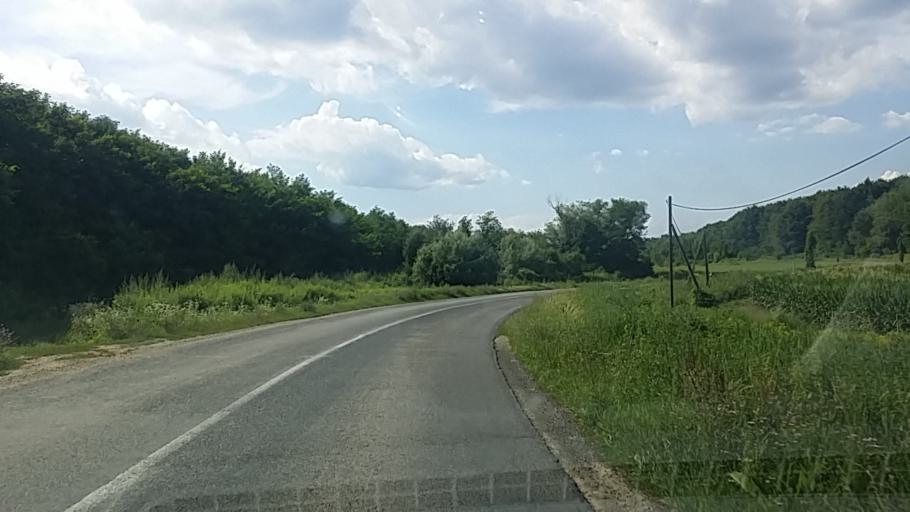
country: HU
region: Zala
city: Becsehely
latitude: 46.4654
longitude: 16.8034
